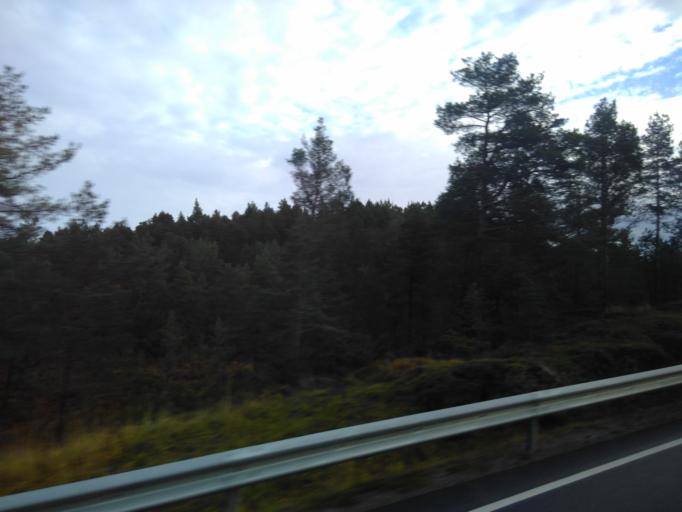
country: NO
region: Sor-Trondelag
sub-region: Hitra
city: Fillan
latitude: 63.5721
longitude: 9.0286
